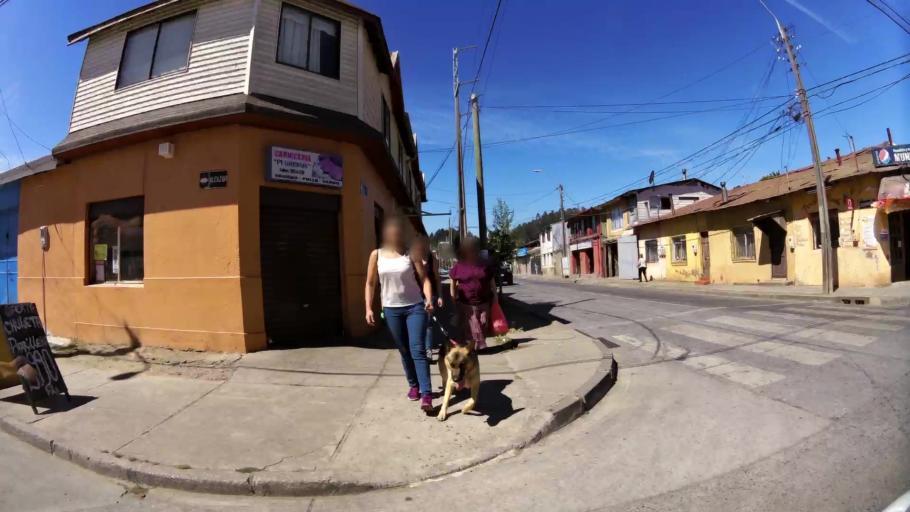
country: CL
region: Biobio
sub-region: Provincia de Concepcion
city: Penco
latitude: -36.7345
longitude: -72.9906
